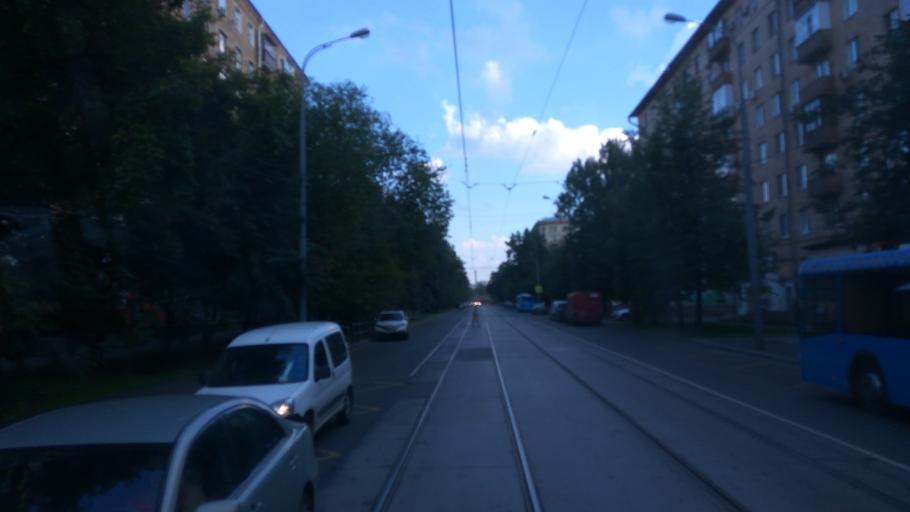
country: RU
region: Moscow
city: Likhobory
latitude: 55.8119
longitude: 37.5725
